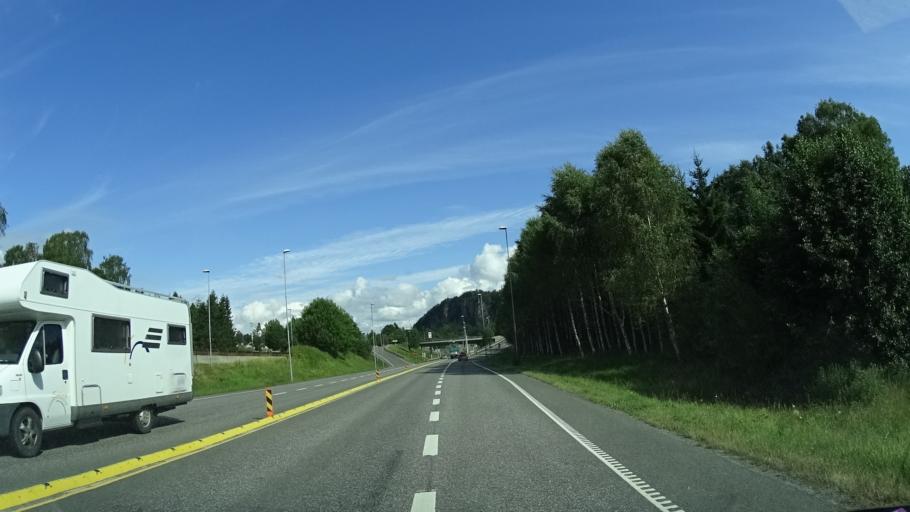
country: NO
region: Telemark
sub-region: Bamble
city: Langesund
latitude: 59.0333
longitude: 9.6772
